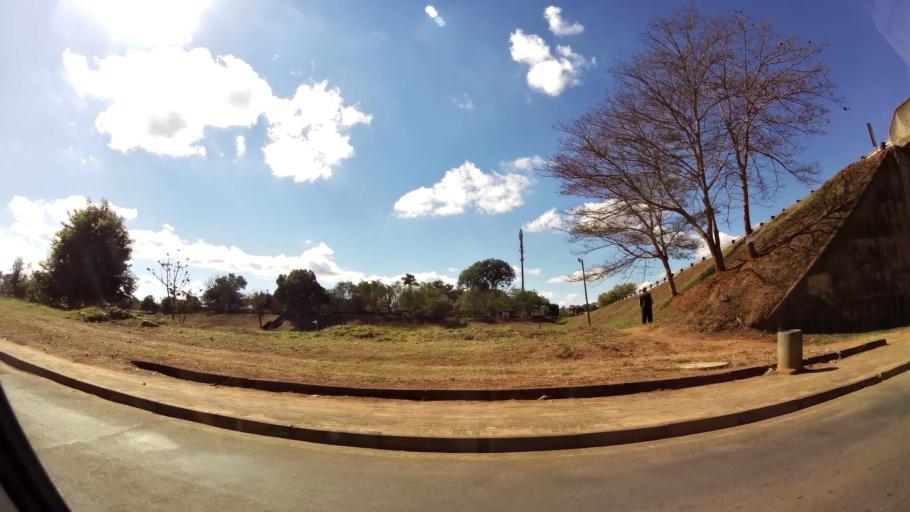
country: ZA
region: Limpopo
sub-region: Mopani District Municipality
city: Tzaneen
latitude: -23.8208
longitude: 30.1626
